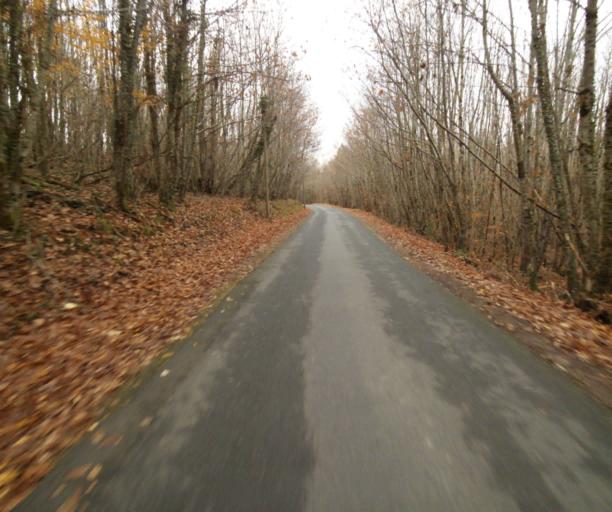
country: FR
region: Limousin
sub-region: Departement de la Correze
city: Laguenne
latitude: 45.2337
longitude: 1.7603
